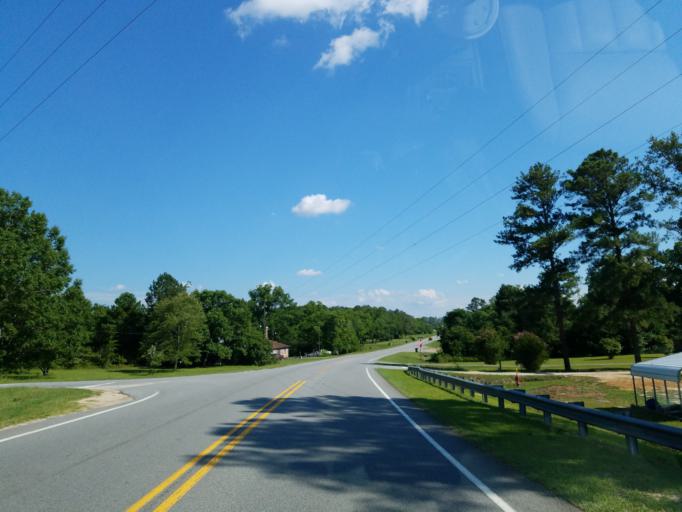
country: US
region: Georgia
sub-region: Crawford County
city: Roberta
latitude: 32.6763
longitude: -84.0040
